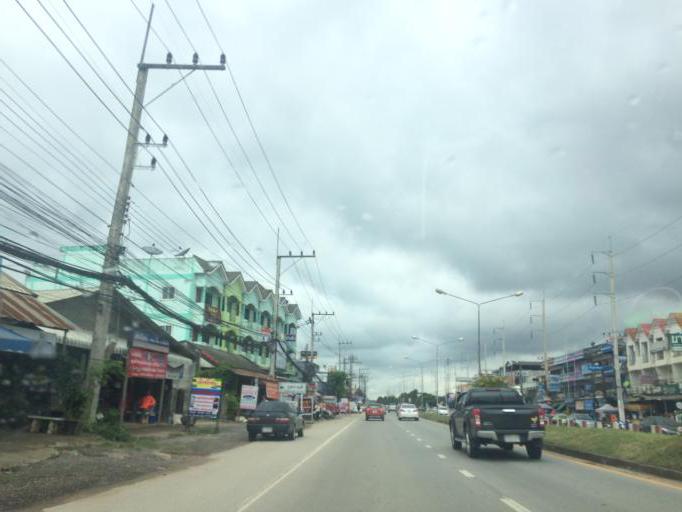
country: TH
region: Chiang Rai
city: Mae Chan
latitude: 20.0478
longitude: 99.8760
